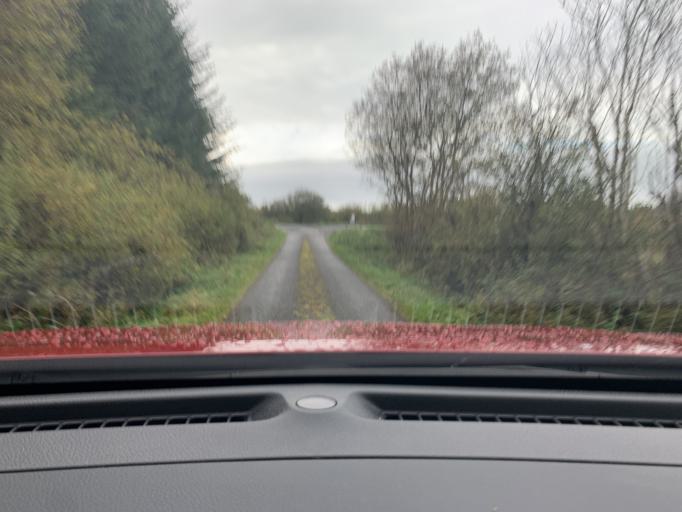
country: IE
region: Connaught
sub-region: Roscommon
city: Ballaghaderreen
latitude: 53.9221
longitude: -8.5710
